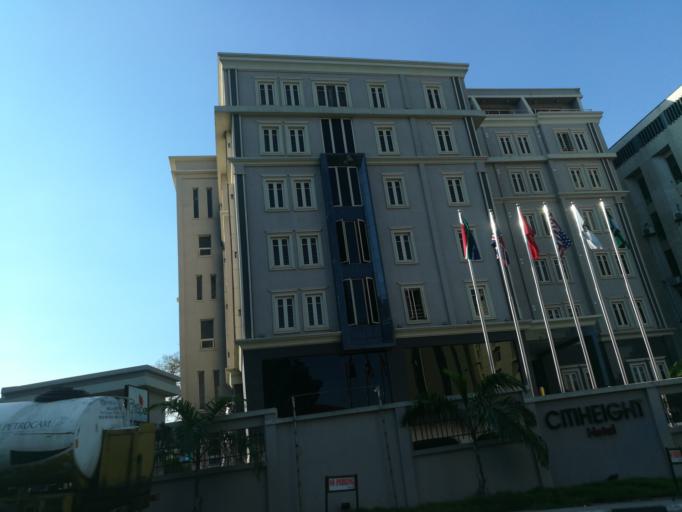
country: NG
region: Lagos
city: Ojota
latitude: 6.5846
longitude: 3.3614
